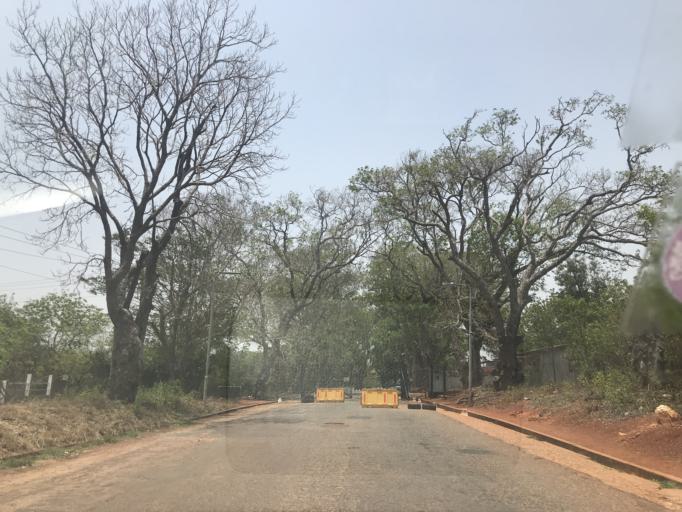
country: GH
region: Greater Accra
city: Teshi Old Town
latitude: 5.5804
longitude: -0.1551
